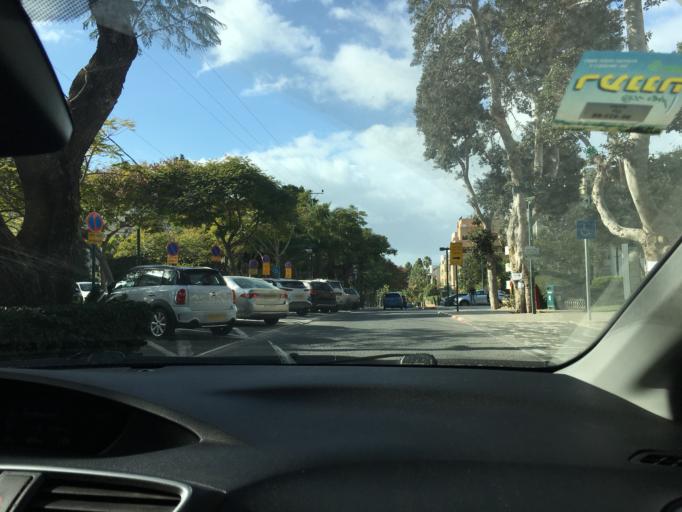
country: IL
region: Tel Aviv
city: Ramat HaSharon
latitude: 32.1444
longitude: 34.8439
